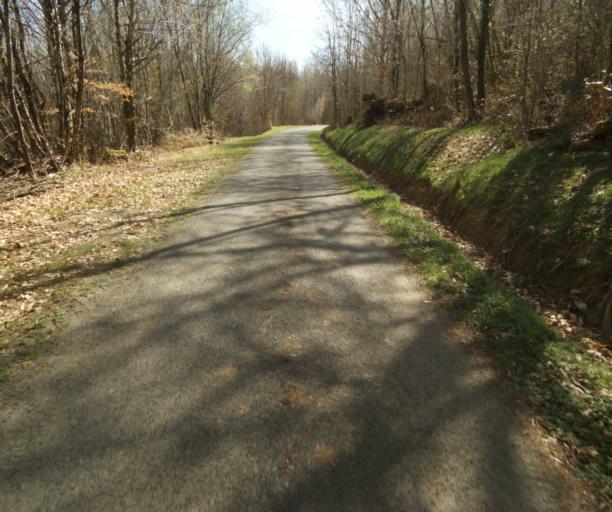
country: FR
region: Limousin
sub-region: Departement de la Correze
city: Seilhac
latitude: 45.3963
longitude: 1.7673
